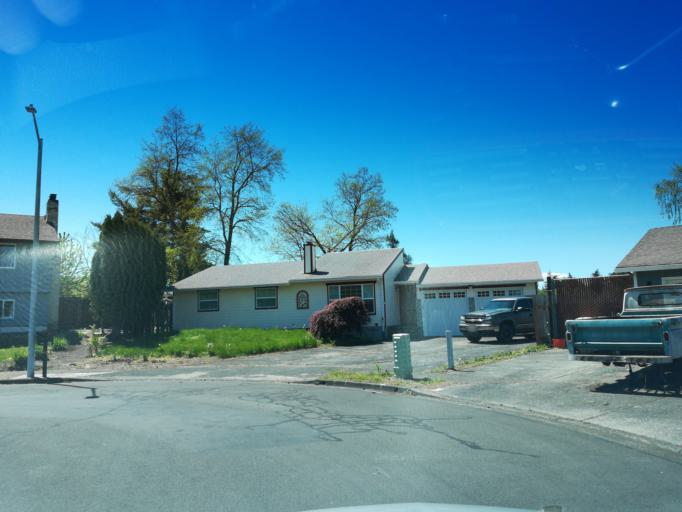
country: US
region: Oregon
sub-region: Multnomah County
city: Troutdale
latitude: 45.5226
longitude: -122.3801
